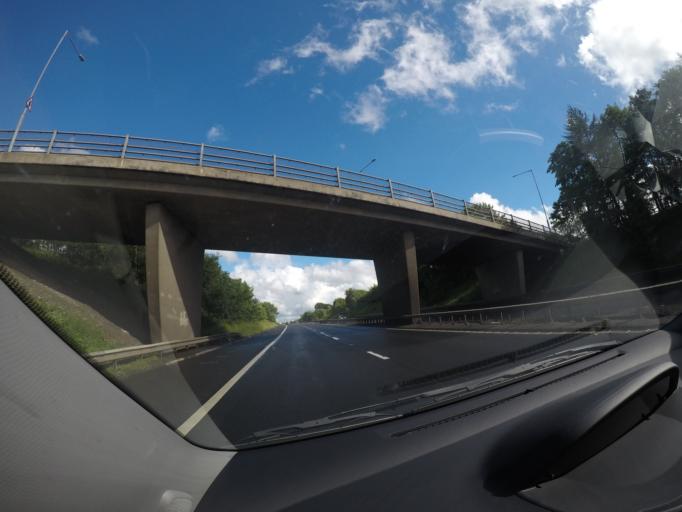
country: GB
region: Scotland
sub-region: South Lanarkshire
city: Lesmahagow
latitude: 55.6376
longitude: -3.8736
